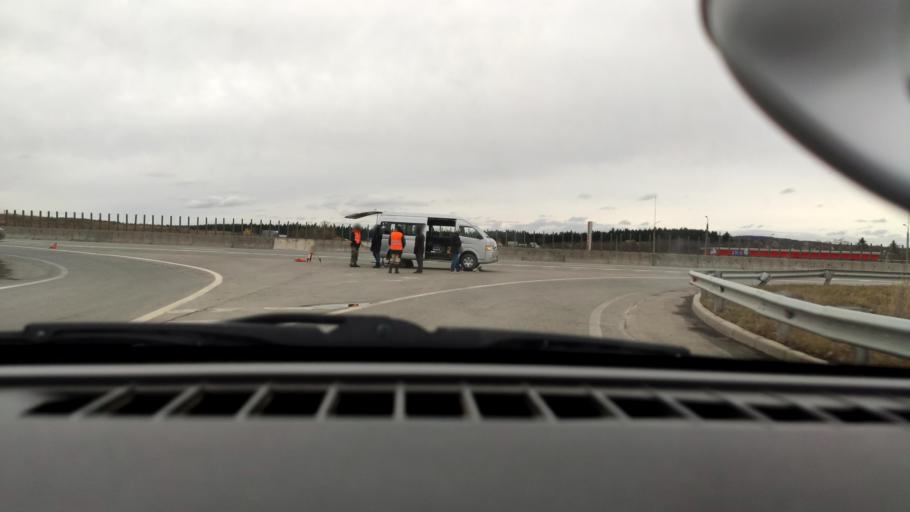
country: RU
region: Perm
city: Ferma
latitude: 57.9302
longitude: 56.3297
